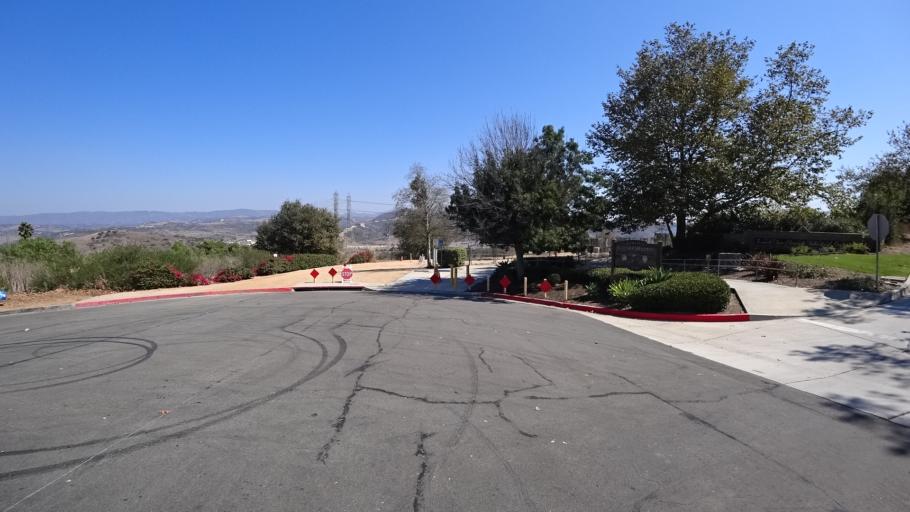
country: US
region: California
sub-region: Orange County
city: San Clemente
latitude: 33.4459
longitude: -117.5817
